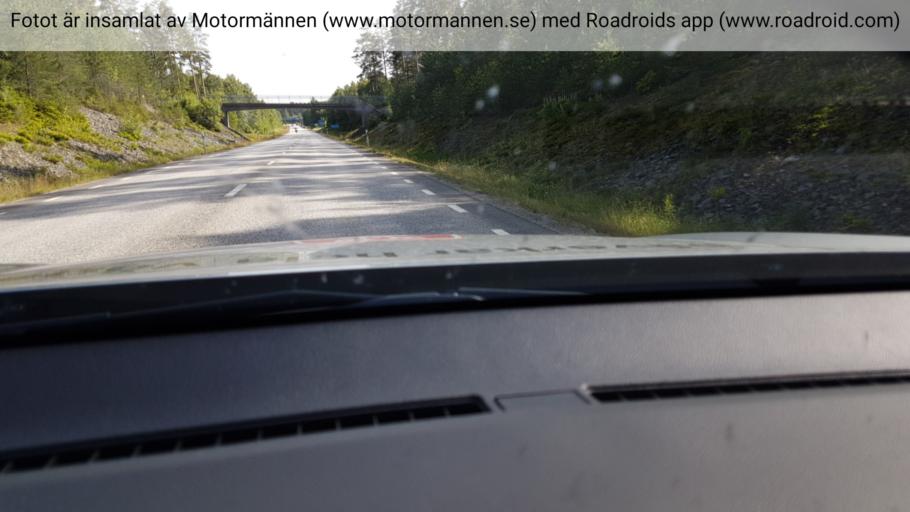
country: SE
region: Joenkoeping
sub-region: Eksjo Kommun
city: Eksjoe
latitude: 57.6854
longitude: 14.9545
